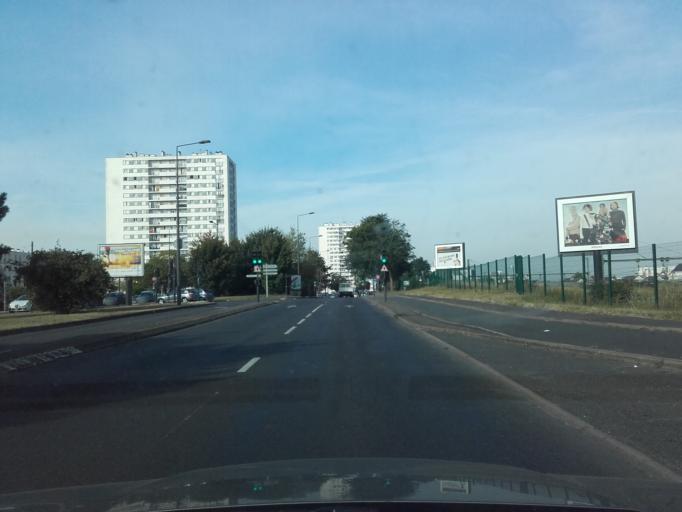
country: FR
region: Centre
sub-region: Departement d'Indre-et-Loire
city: Tours
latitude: 47.3734
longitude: 0.6899
